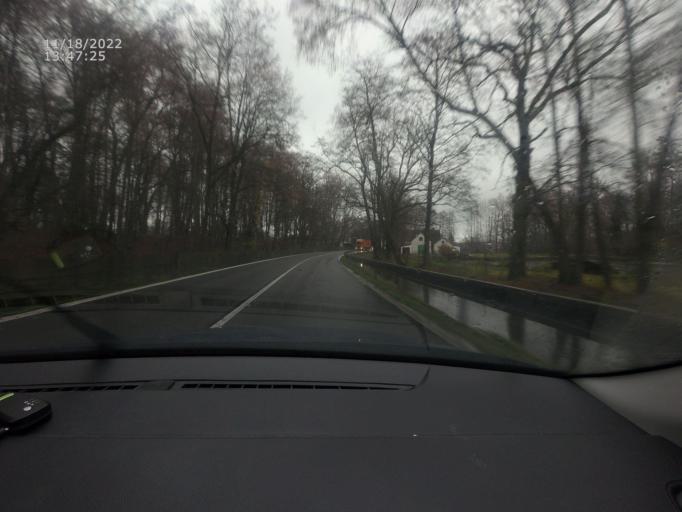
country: CZ
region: Jihocesky
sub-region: Okres Strakonice
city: Blatna
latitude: 49.4226
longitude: 13.8745
